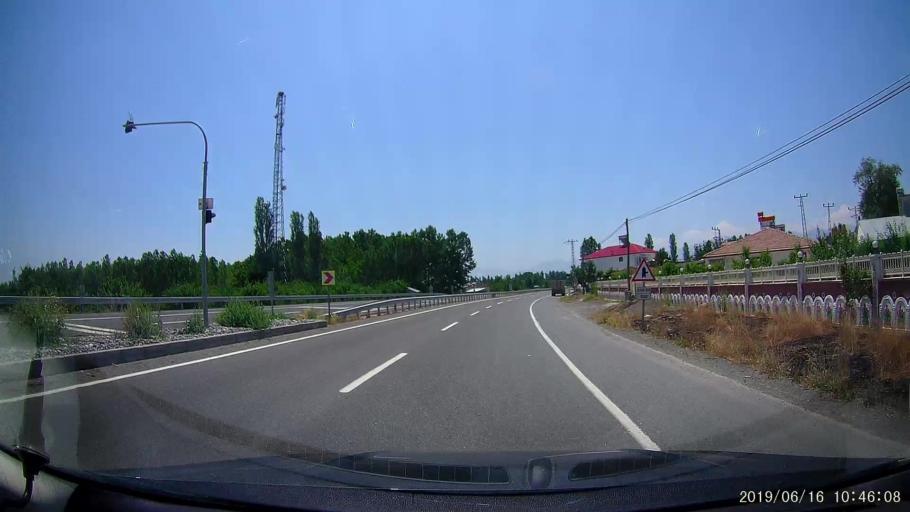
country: AM
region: Armavir
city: Shenavan
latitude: 40.0246
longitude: 43.8772
